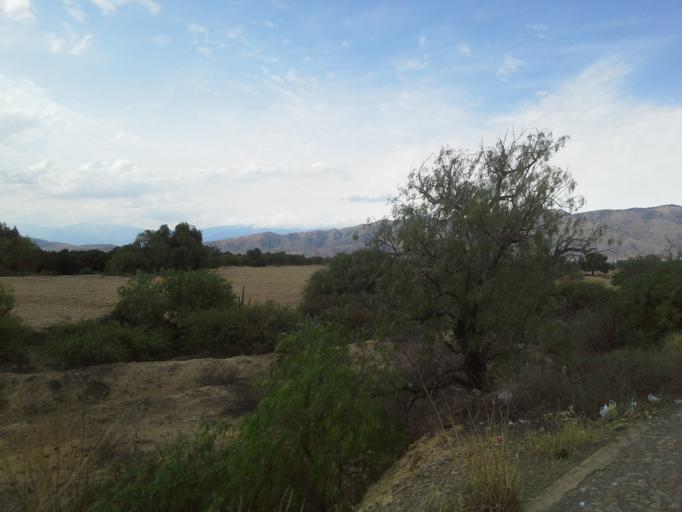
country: BO
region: Cochabamba
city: Tarata
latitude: -17.6049
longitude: -66.0210
